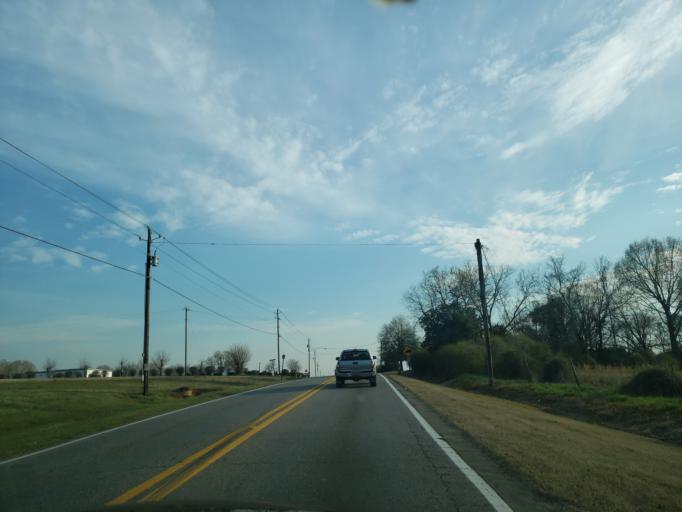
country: US
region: Alabama
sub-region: Hale County
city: Moundville
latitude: 32.9925
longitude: -87.6244
